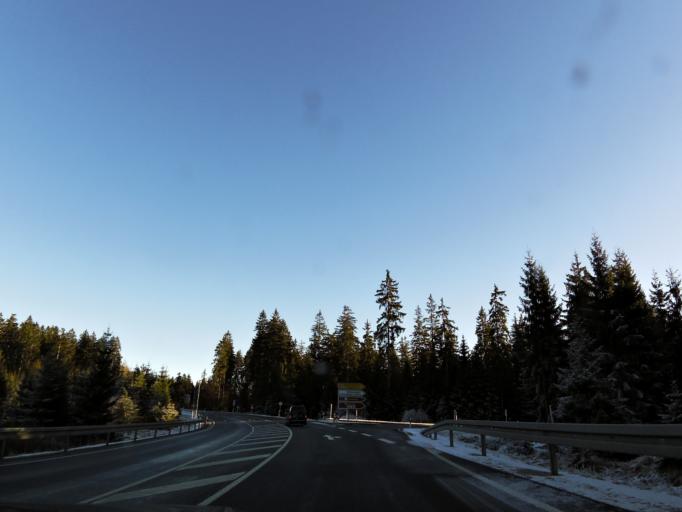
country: DE
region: Bavaria
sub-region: Upper Franconia
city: Fichtelberg
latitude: 50.0287
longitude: 11.8538
